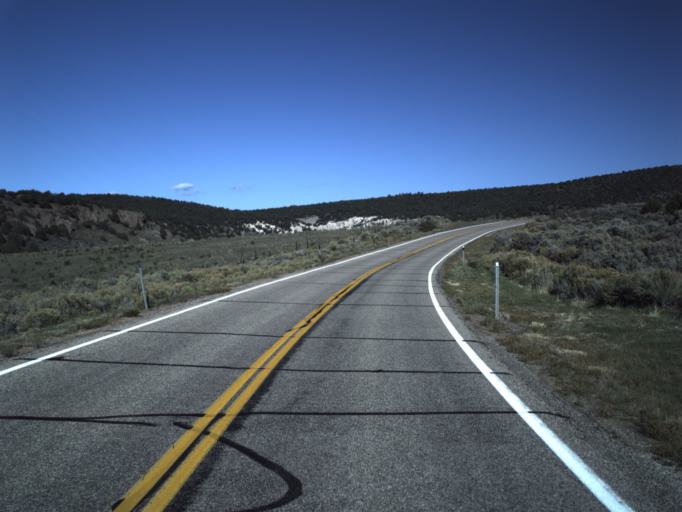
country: US
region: Utah
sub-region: Garfield County
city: Panguitch
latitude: 37.7673
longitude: -112.5497
